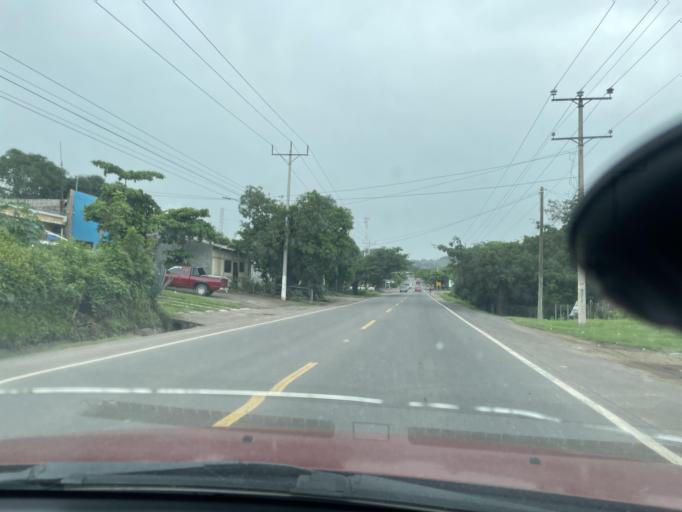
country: SV
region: San Miguel
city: San Miguel
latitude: 13.5138
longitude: -88.1471
